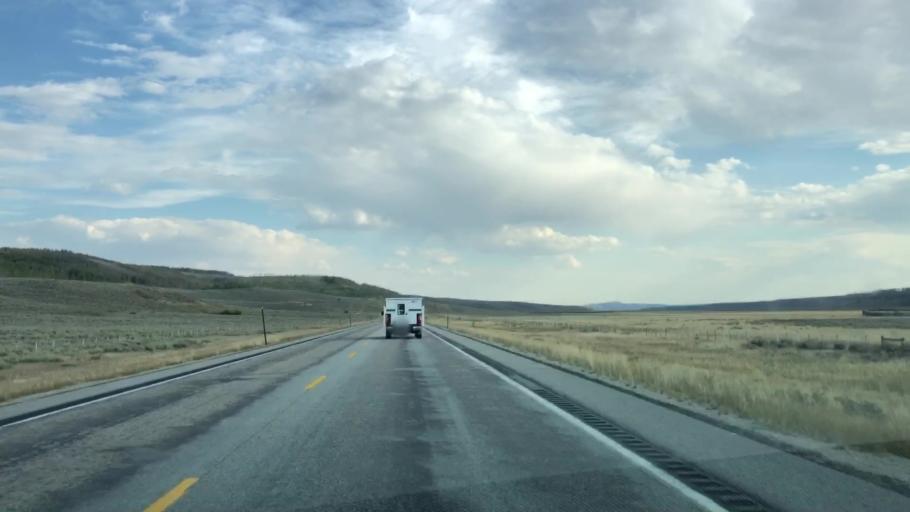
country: US
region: Wyoming
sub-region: Sublette County
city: Pinedale
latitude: 43.1013
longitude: -110.1695
